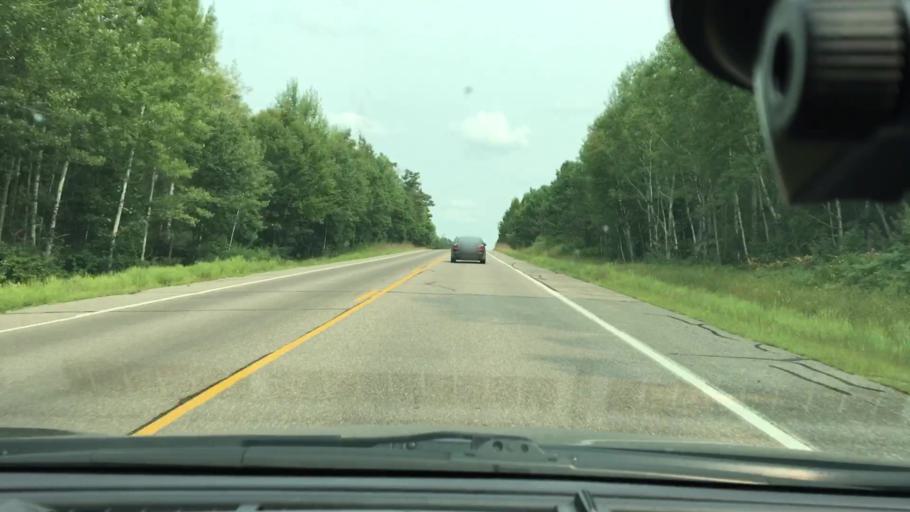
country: US
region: Minnesota
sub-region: Crow Wing County
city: Cross Lake
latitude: 46.7308
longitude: -93.9924
